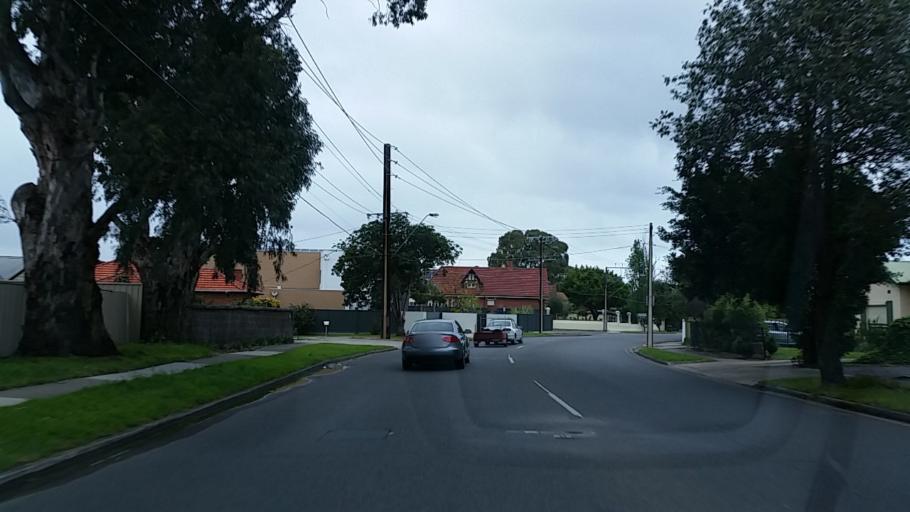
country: AU
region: South Australia
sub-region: Charles Sturt
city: Findon
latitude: -34.9251
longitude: 138.5357
